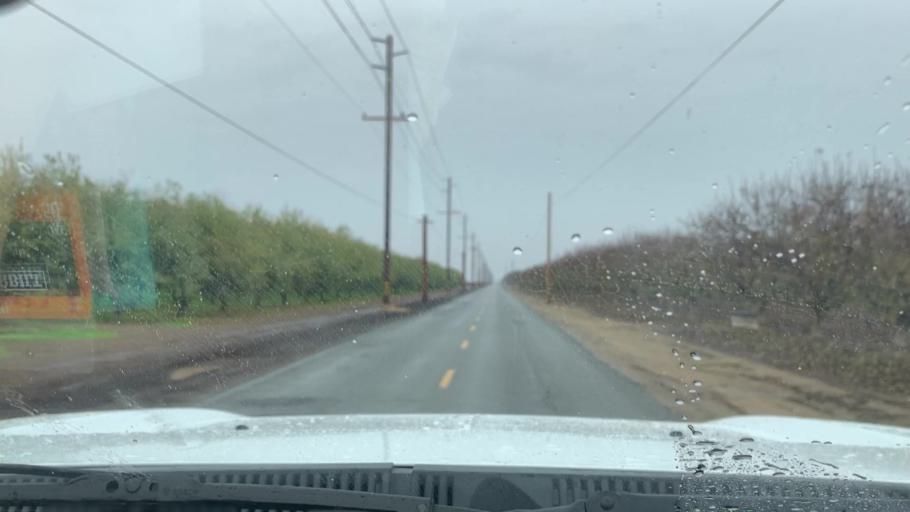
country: US
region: California
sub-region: Kern County
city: Delano
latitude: 35.8341
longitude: -119.1916
